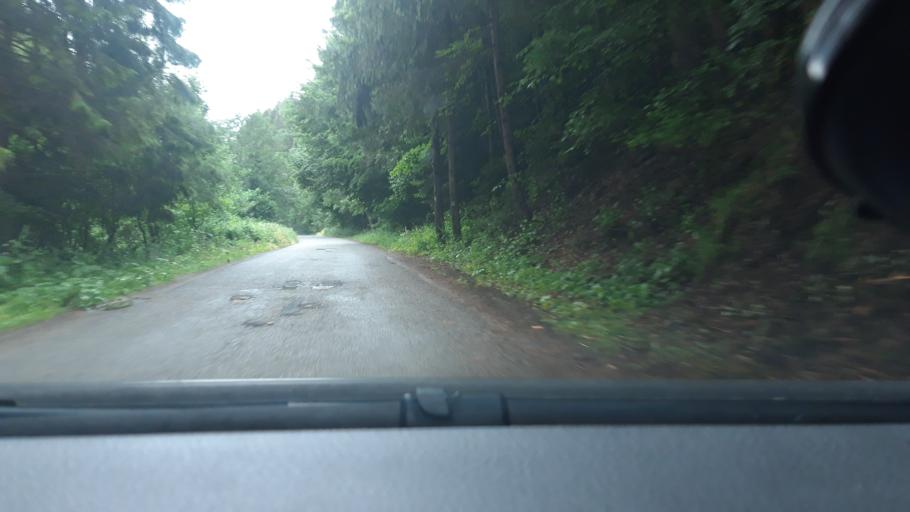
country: SK
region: Zilinsky
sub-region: Okres Martin
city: Martin
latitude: 49.0091
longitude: 18.9961
